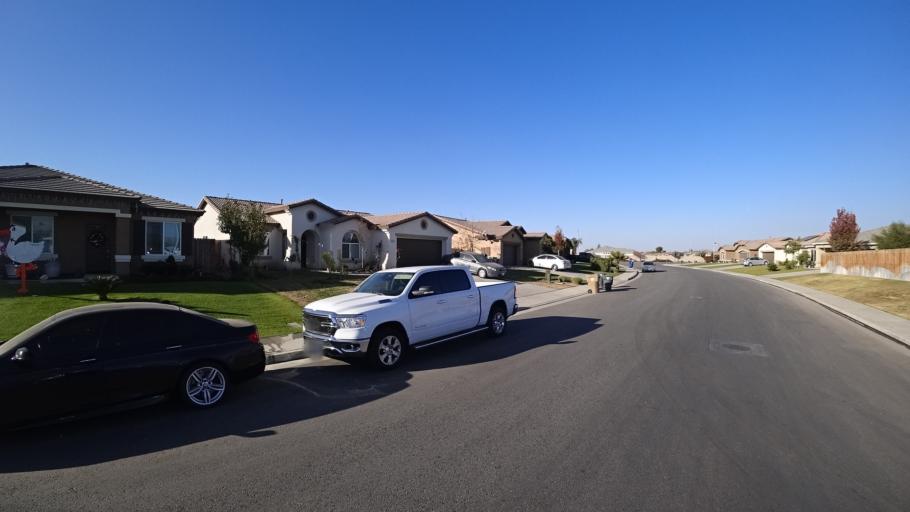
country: US
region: California
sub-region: Kern County
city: Greenfield
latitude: 35.2713
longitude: -119.0289
